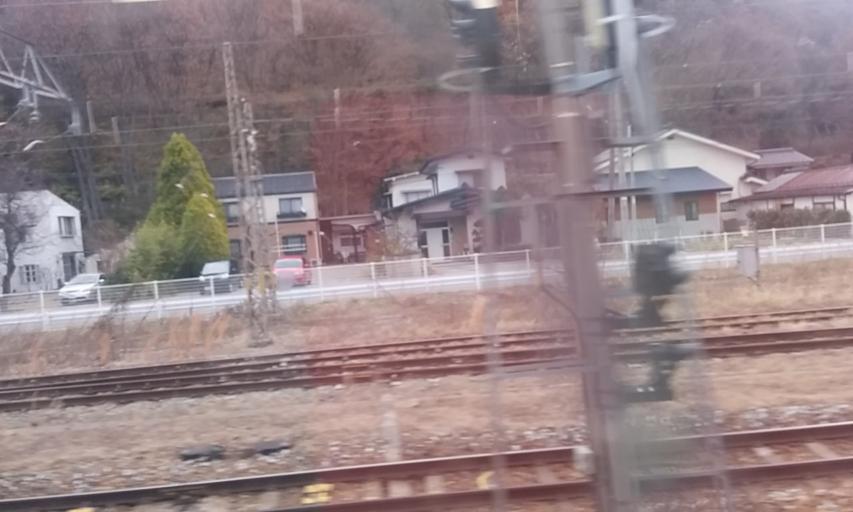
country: JP
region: Nagano
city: Nagano-shi
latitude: 36.5330
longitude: 138.1281
